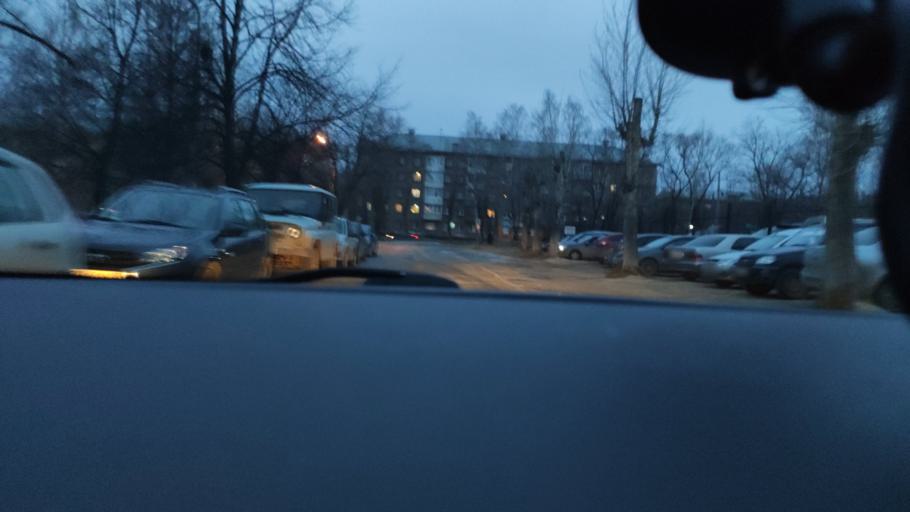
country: RU
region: Perm
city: Froly
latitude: 57.9592
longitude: 56.2449
